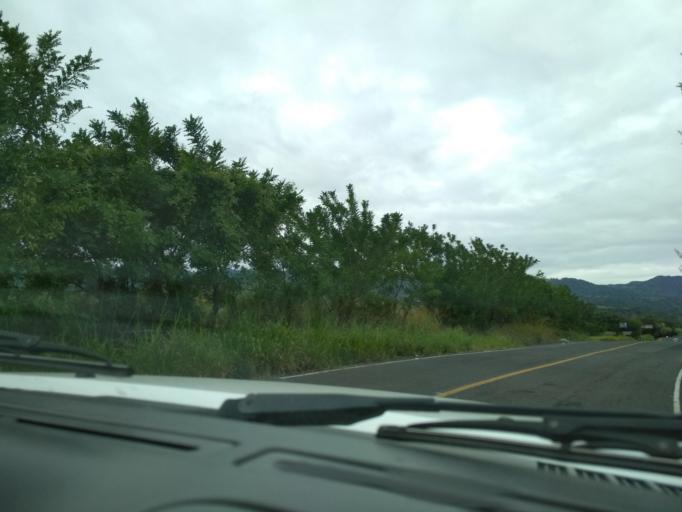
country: MX
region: Veracruz
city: El Castillo
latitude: 19.5822
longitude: -96.8172
